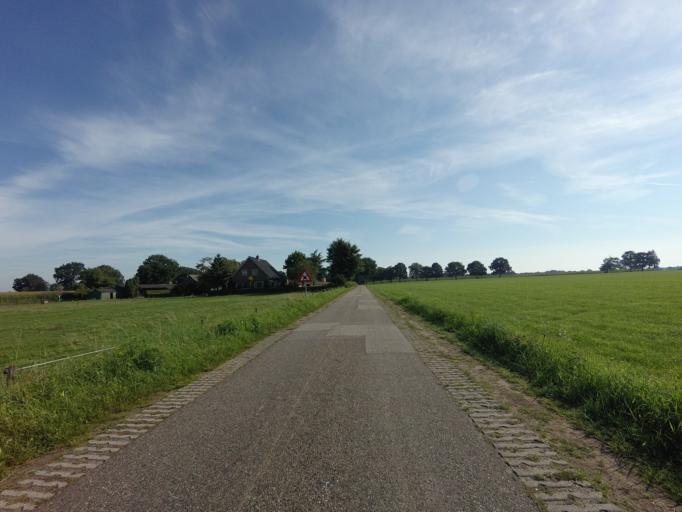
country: NL
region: Gelderland
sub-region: Oude IJsselstreek
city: Varsseveld
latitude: 51.9706
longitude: 6.4840
